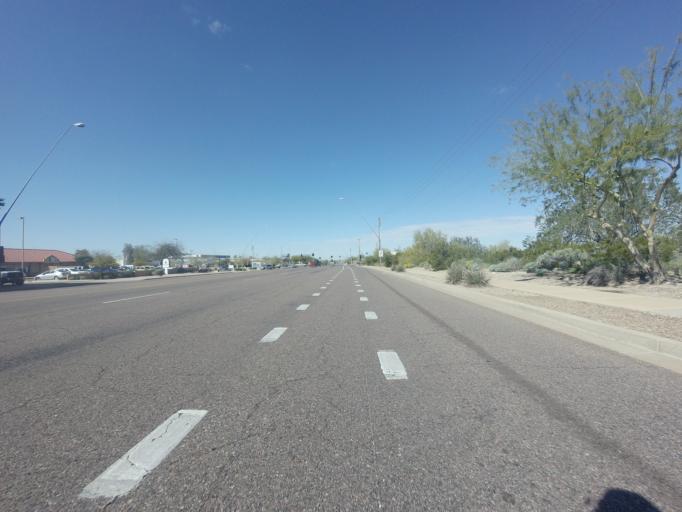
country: US
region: Arizona
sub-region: Maricopa County
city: Mesa
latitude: 33.4665
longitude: -111.6995
